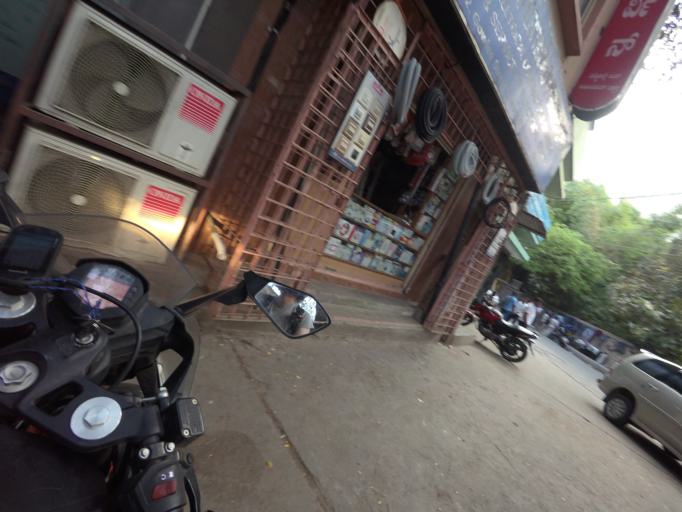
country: IN
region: Karnataka
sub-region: Bangalore Urban
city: Bangalore
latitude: 12.9751
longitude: 77.6218
